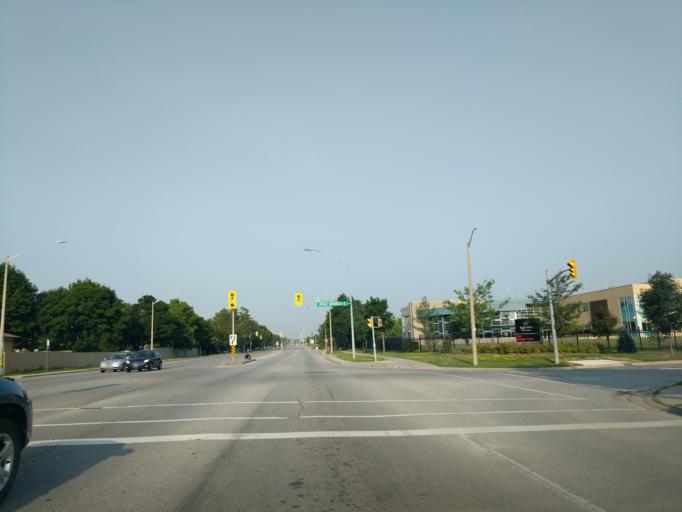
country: CA
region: Ontario
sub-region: York
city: Richmond Hill
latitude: 43.8933
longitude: -79.4247
